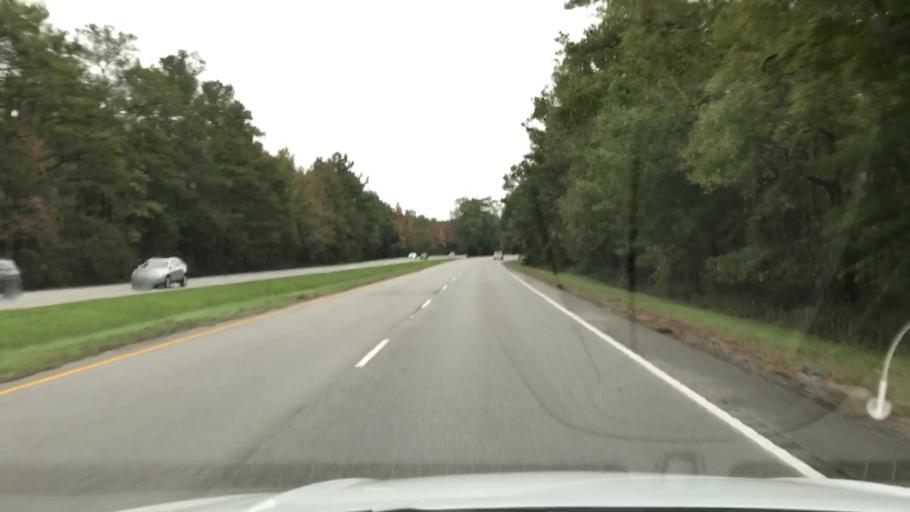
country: US
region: South Carolina
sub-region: Georgetown County
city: Georgetown
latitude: 33.4010
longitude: -79.2004
